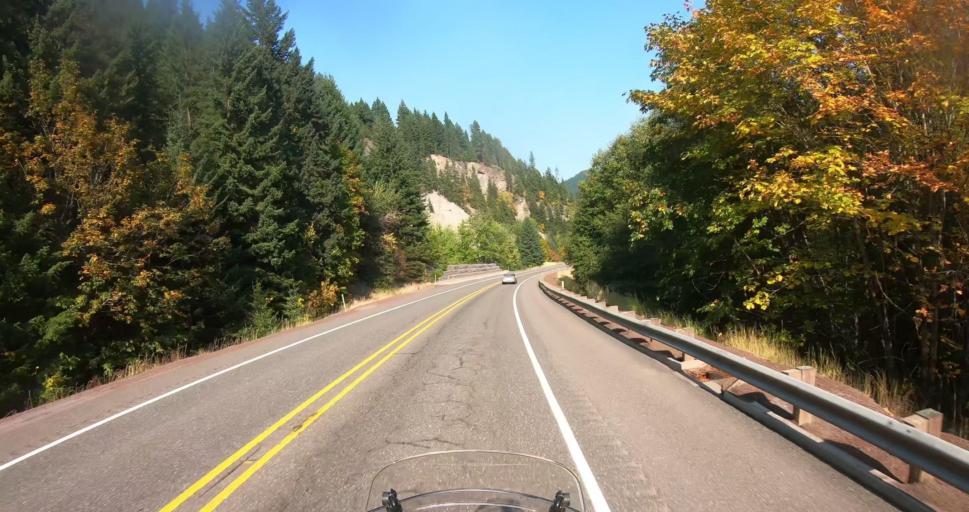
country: US
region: Oregon
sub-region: Hood River County
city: Odell
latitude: 45.4623
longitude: -121.5790
